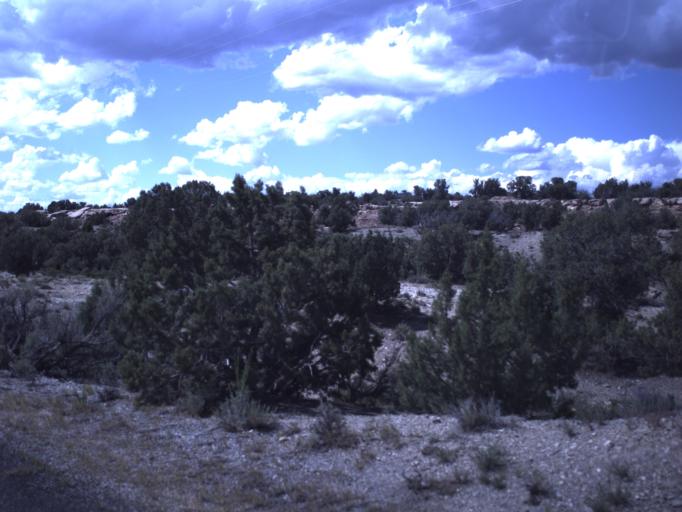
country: US
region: Utah
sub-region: Duchesne County
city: Duchesne
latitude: 40.1773
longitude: -110.4482
